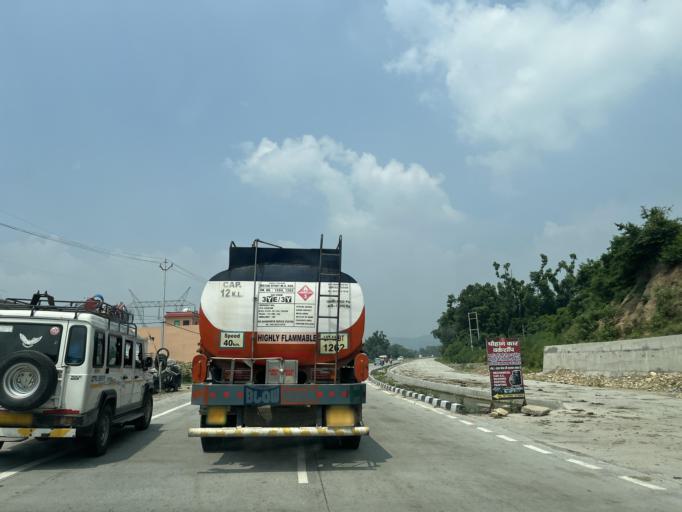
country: IN
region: Uttarakhand
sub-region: Haridwar
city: Haridwar
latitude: 29.8486
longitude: 78.1852
